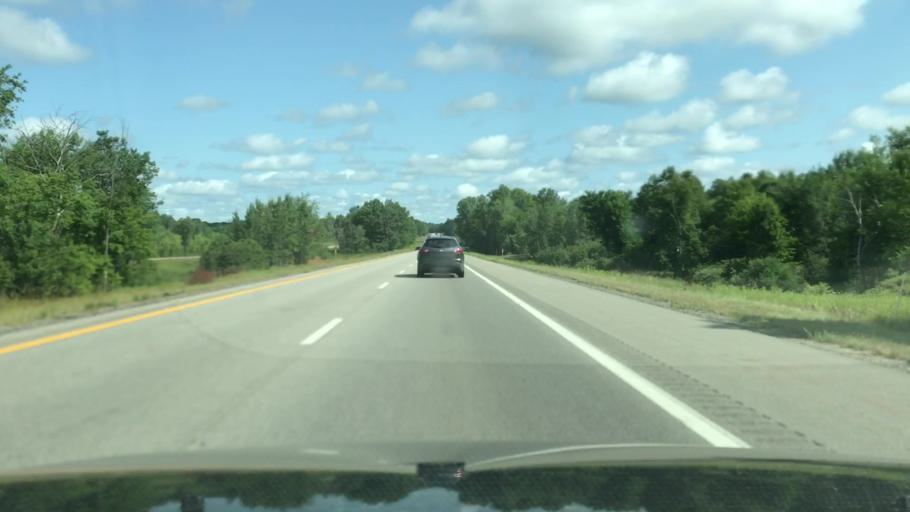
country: US
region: Michigan
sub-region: Montcalm County
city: Howard City
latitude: 43.5331
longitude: -85.4861
